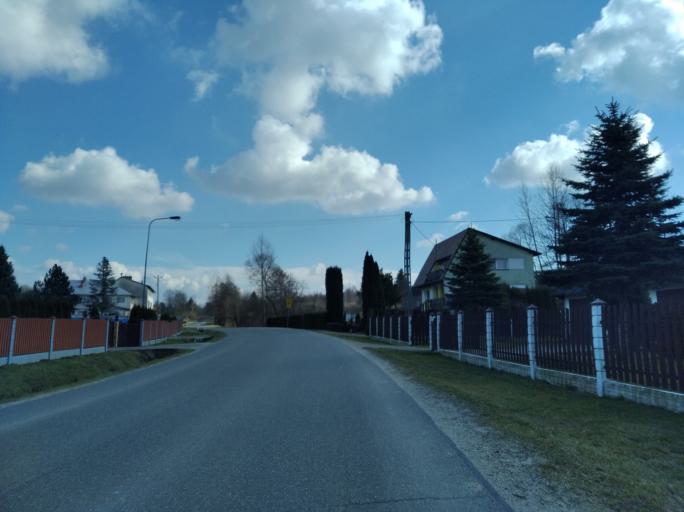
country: PL
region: Subcarpathian Voivodeship
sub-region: Powiat jasielski
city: Kolaczyce
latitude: 49.8539
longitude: 21.4981
